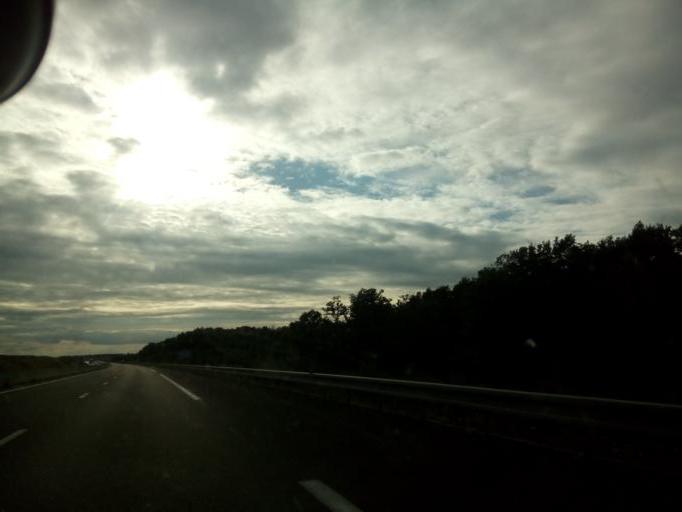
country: FR
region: Centre
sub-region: Departement d'Indre-et-Loire
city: Veigne
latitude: 47.3139
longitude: 0.7512
